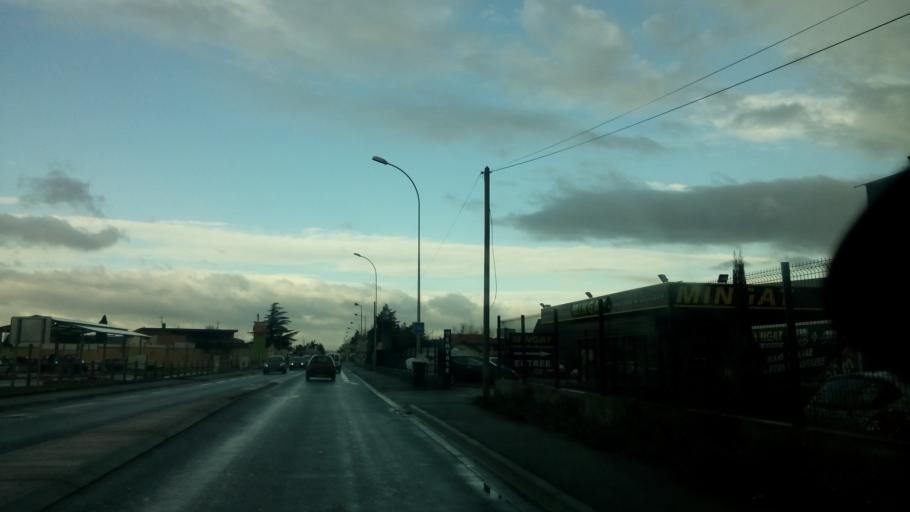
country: FR
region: Rhone-Alpes
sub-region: Departement du Rhone
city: Mions
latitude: 45.6809
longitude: 4.9578
